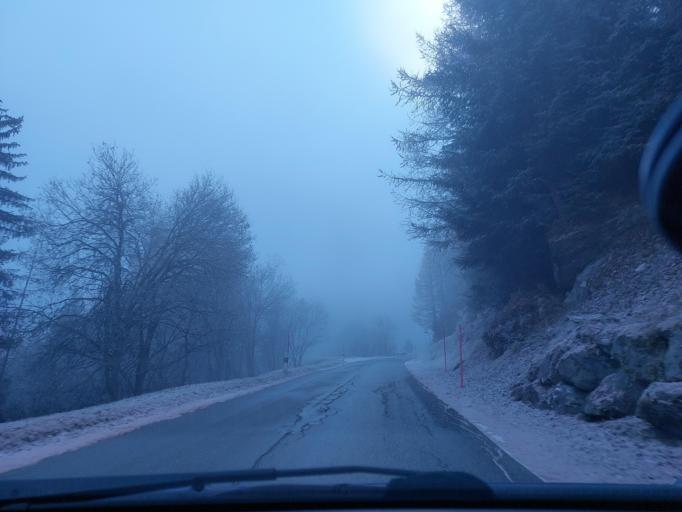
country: CH
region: Valais
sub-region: Conthey District
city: Basse-Nendaz
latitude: 46.1427
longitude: 7.3158
